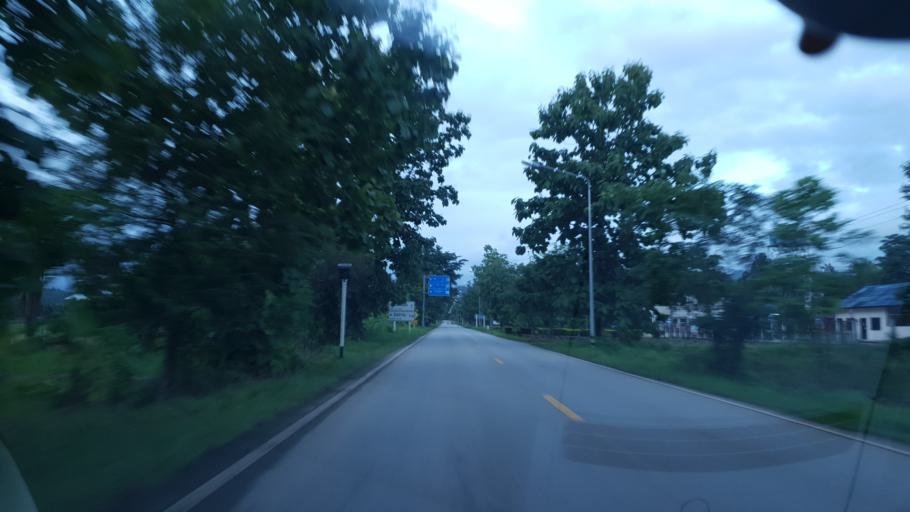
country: TH
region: Mae Hong Son
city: Mae La Noi
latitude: 18.3346
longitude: 97.9153
